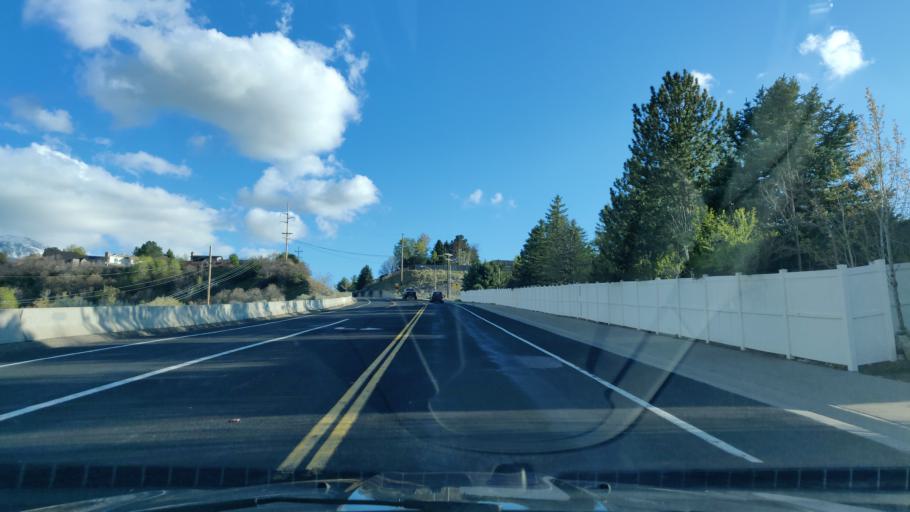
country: US
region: Utah
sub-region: Salt Lake County
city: Cottonwood Heights
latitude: 40.6299
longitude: -111.8074
